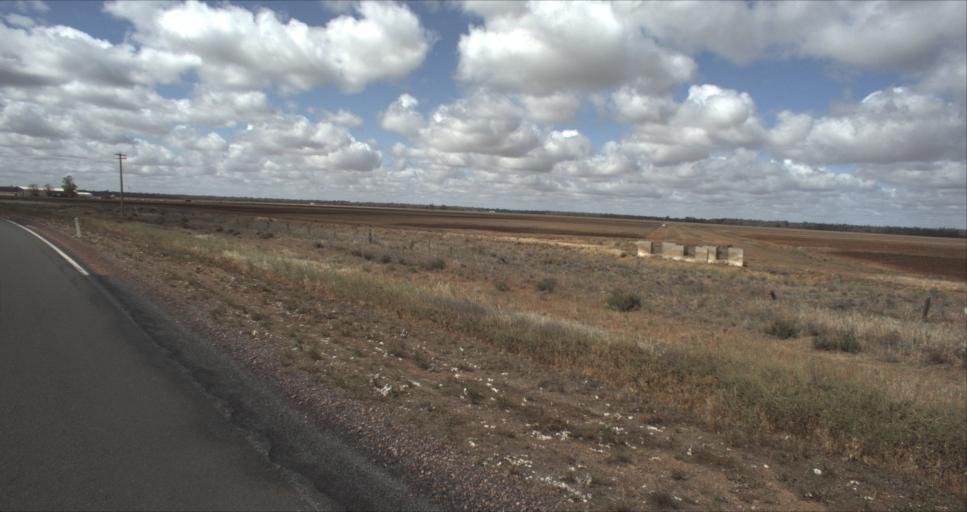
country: AU
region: New South Wales
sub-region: Murrumbidgee Shire
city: Darlington Point
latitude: -34.5834
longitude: 146.1143
